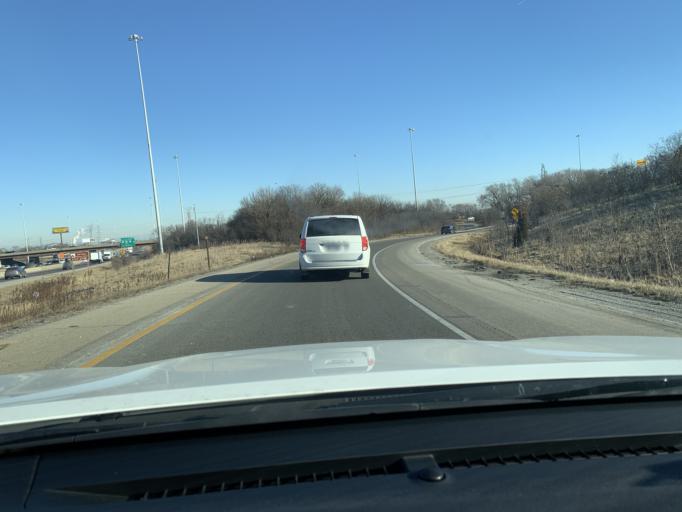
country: US
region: Illinois
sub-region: Cook County
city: Hodgkins
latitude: 41.7609
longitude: -87.8710
